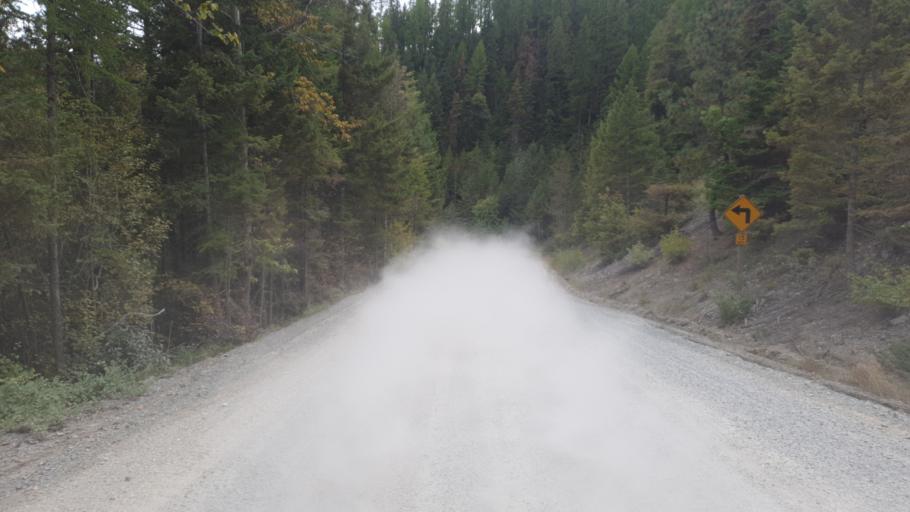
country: US
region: Montana
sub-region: Flathead County
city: Lakeside
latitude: 47.9906
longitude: -114.3189
